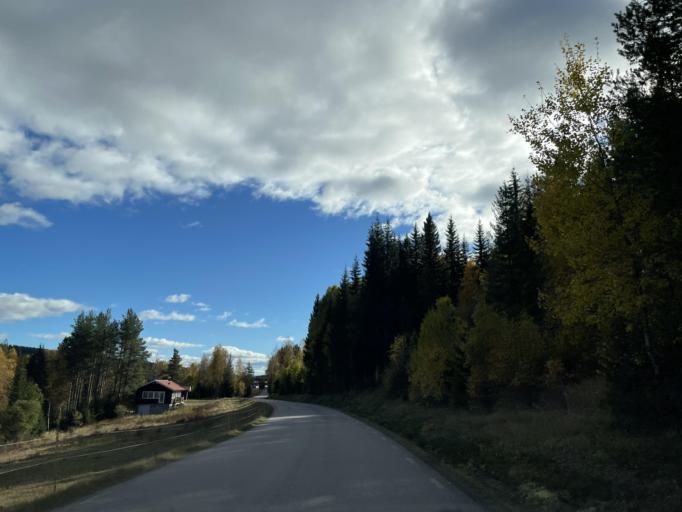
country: SE
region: Dalarna
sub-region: Malung-Saelens kommun
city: Malung
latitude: 61.1346
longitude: 13.2736
